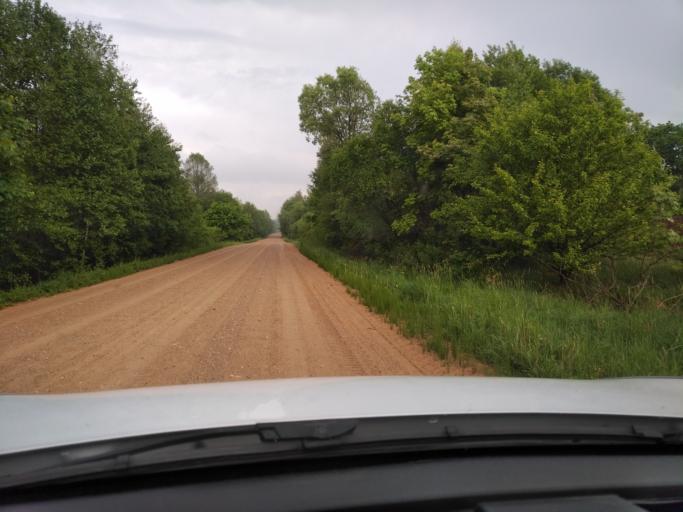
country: LT
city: Ignalina
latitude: 55.2670
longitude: 26.1186
